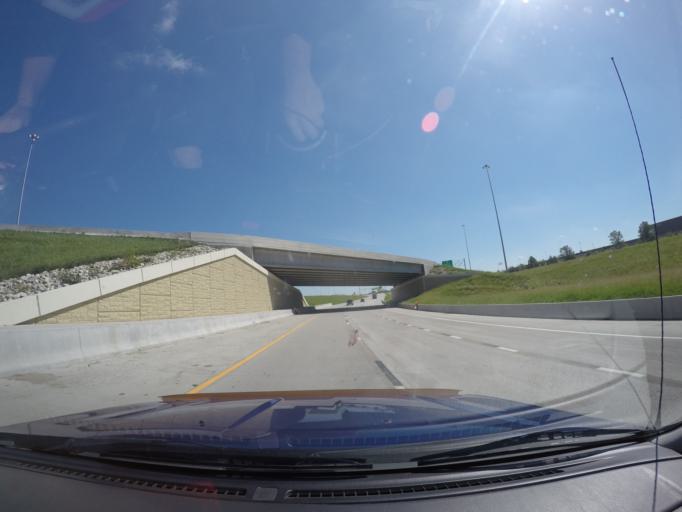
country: US
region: Kansas
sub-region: Johnson County
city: Lenexa
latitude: 38.9431
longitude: -94.7718
